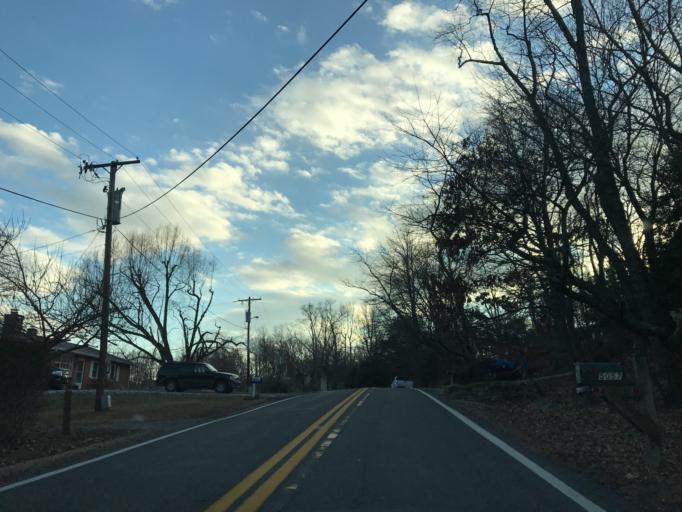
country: US
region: Maryland
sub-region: Cecil County
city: Charlestown
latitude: 39.4678
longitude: -75.9958
